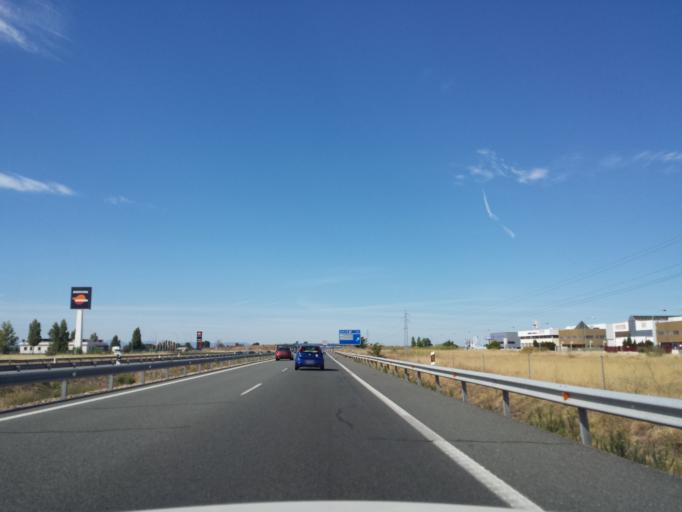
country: ES
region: Castille-La Mancha
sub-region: Province of Toledo
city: Velada
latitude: 39.9545
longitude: -4.9301
